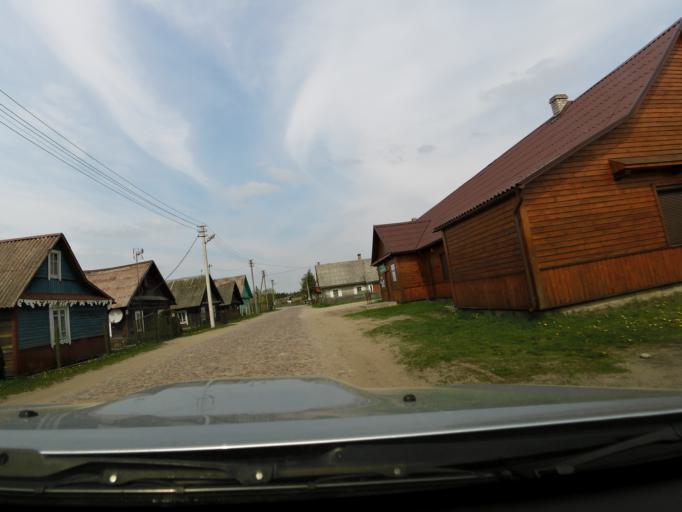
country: LT
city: Baltoji Voke
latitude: 54.4362
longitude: 25.1512
